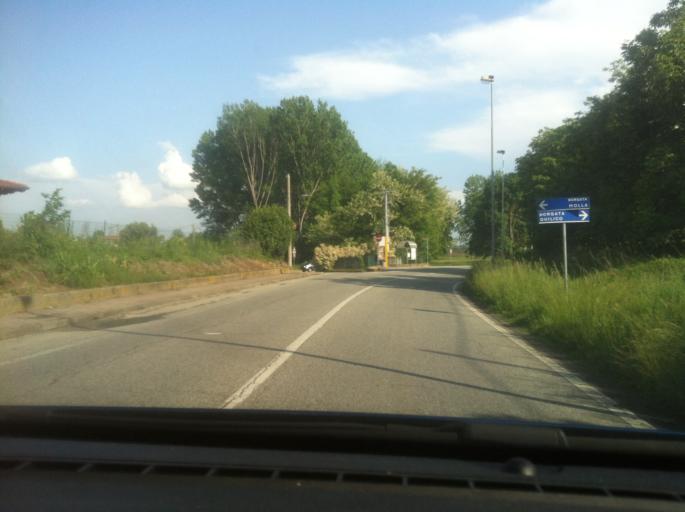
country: IT
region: Piedmont
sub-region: Provincia di Torino
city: Pavone Canavese
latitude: 45.4285
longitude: 7.8582
